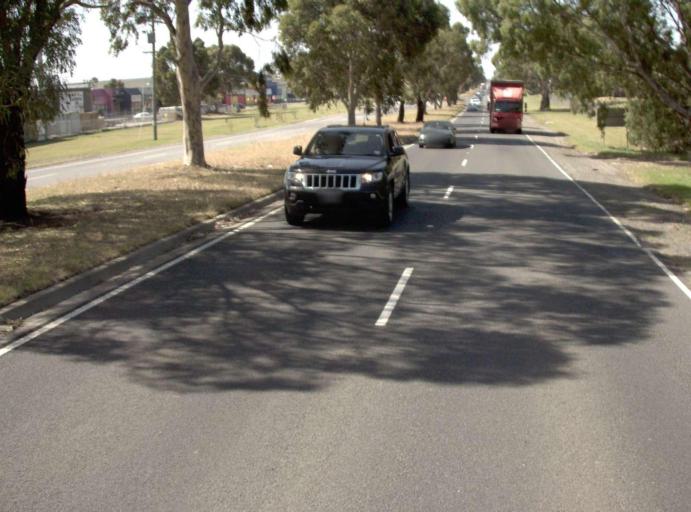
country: AU
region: Victoria
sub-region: Casey
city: Hampton Park
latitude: -38.0366
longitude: 145.2111
